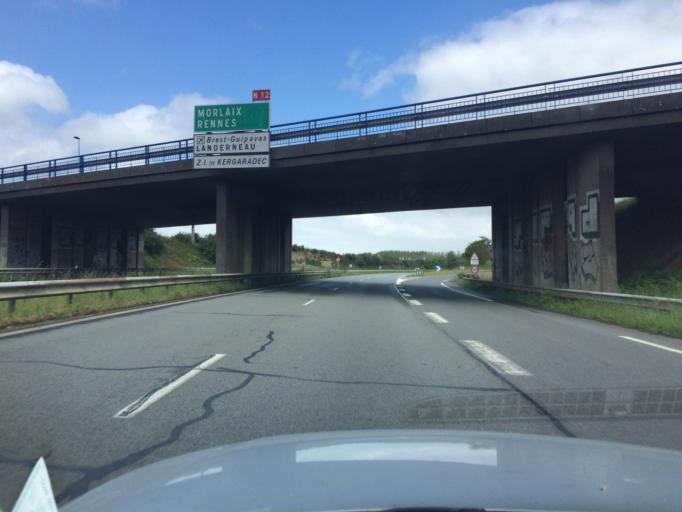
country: FR
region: Brittany
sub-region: Departement du Finistere
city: Gouesnou
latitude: 48.4327
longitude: -4.4685
